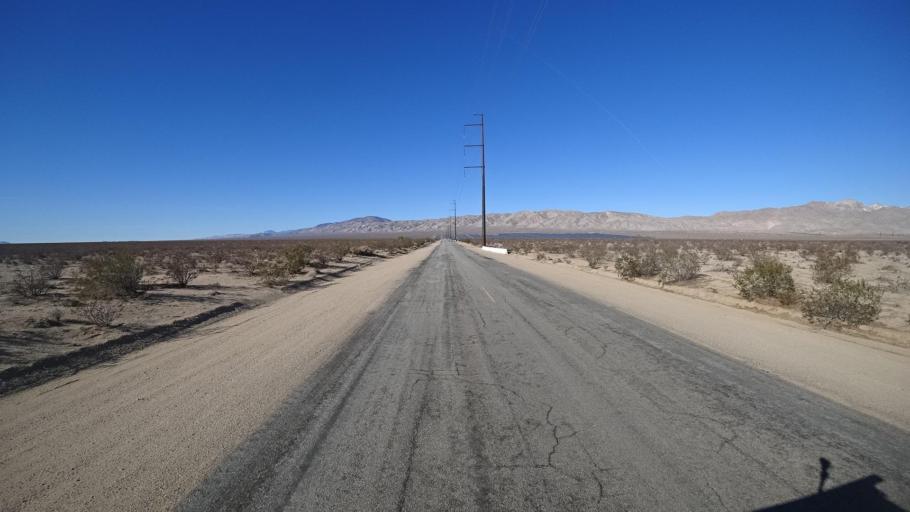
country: US
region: California
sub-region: Kern County
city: California City
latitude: 35.2003
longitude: -118.0377
